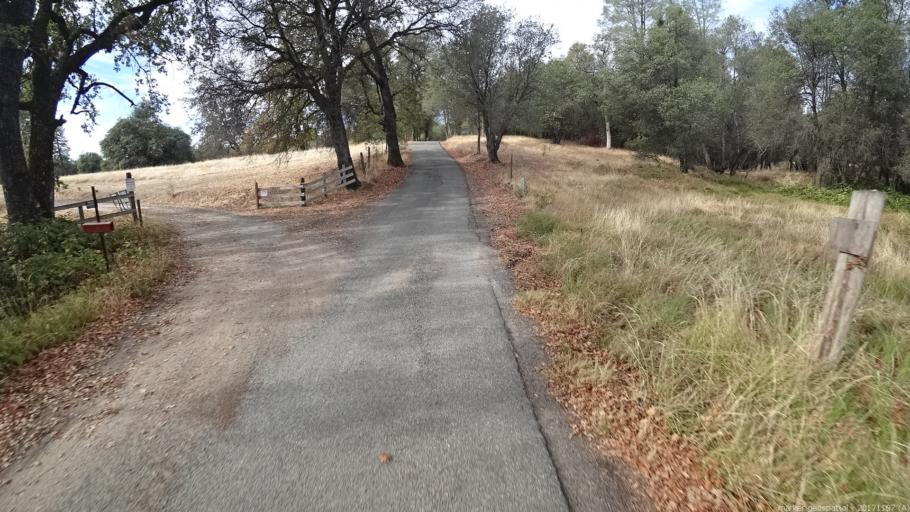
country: US
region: California
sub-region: Shasta County
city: Shasta
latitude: 40.5010
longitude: -122.5950
